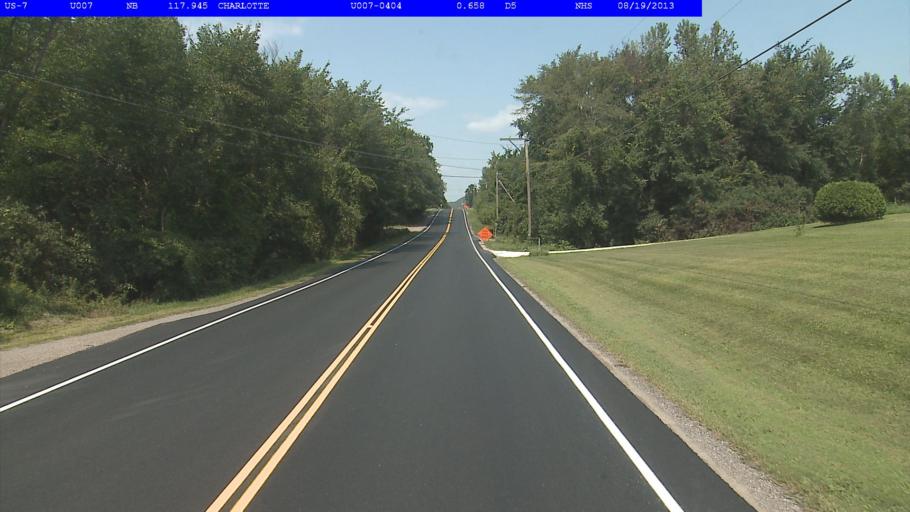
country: US
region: Vermont
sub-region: Addison County
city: Vergennes
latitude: 44.2717
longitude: -73.2336
